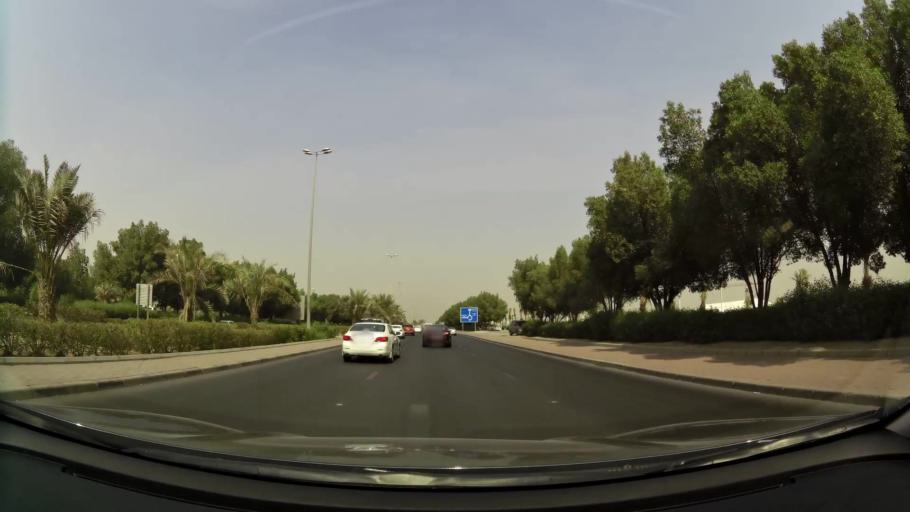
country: KW
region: Al Asimah
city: Ar Rabiyah
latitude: 29.2822
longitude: 47.9068
